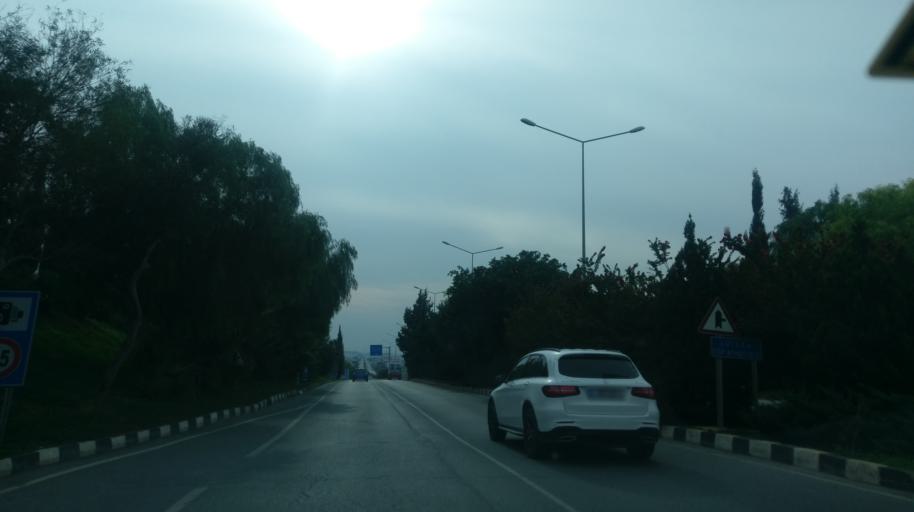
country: CY
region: Keryneia
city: Kyrenia
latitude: 35.2850
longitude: 33.2798
